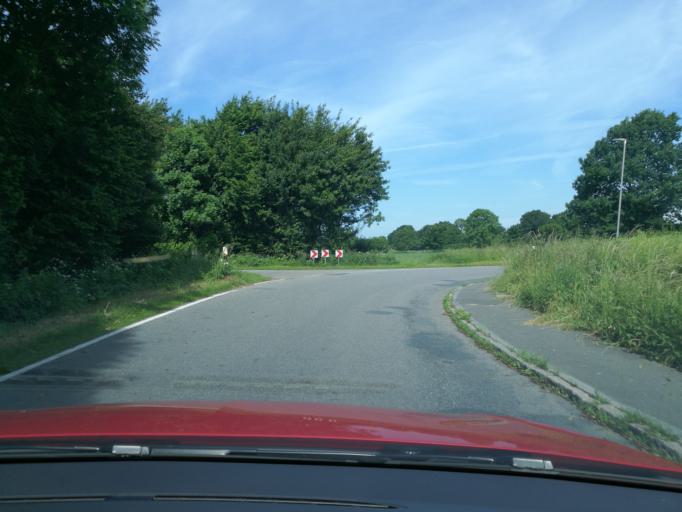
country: DE
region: Schleswig-Holstein
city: Lasbek
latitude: 53.7386
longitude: 10.3447
